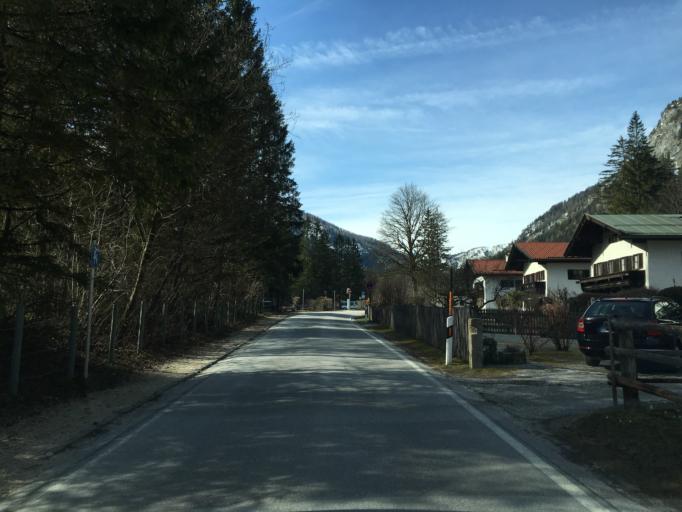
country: DE
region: Bavaria
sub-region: Upper Bavaria
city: Ramsau
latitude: 47.5999
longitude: 12.8442
